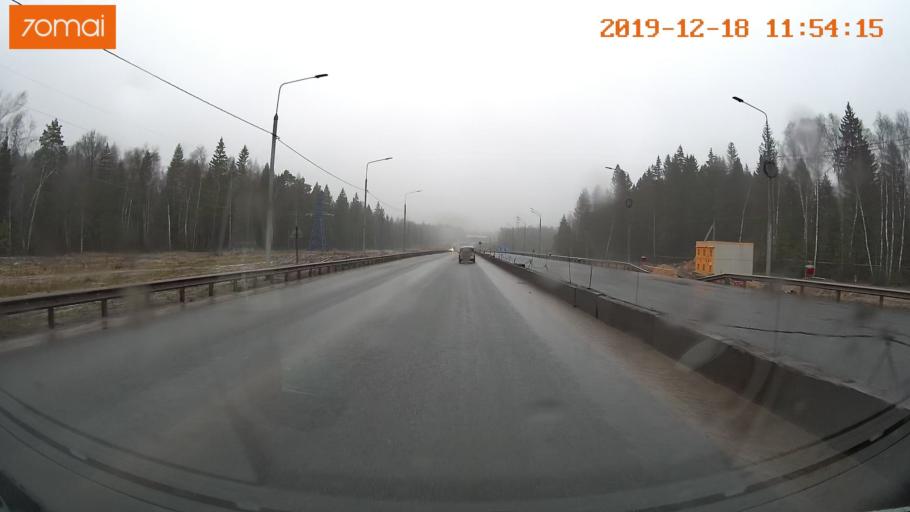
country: RU
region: Moskovskaya
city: Yershovo
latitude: 55.8135
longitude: 36.9185
